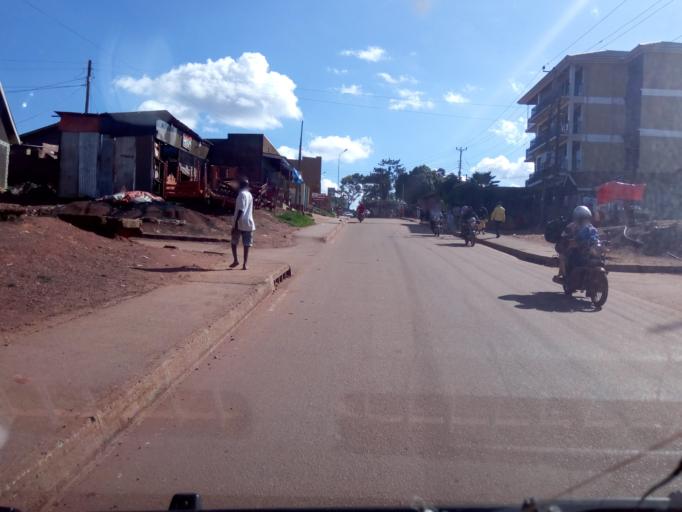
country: UG
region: Central Region
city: Kampala Central Division
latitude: 0.3329
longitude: 32.5572
